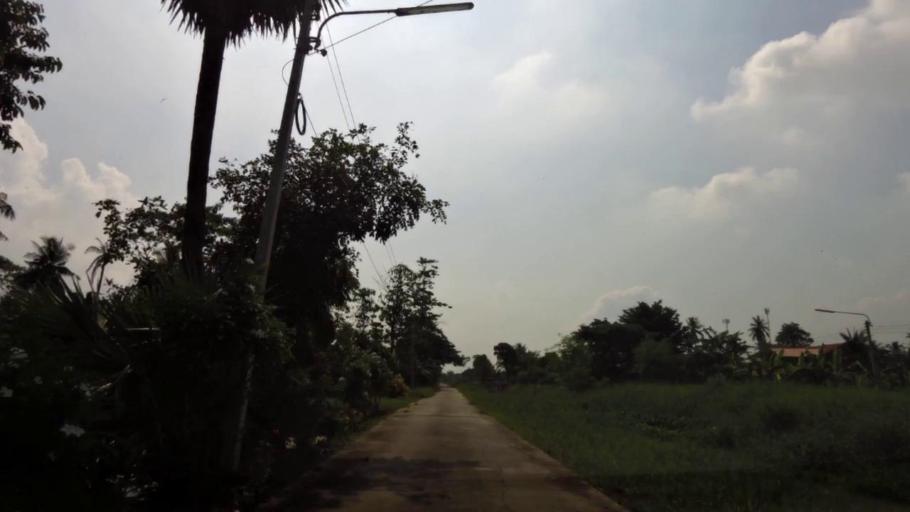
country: TH
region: Ang Thong
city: Wiset Chaichan
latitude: 14.6070
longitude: 100.3929
